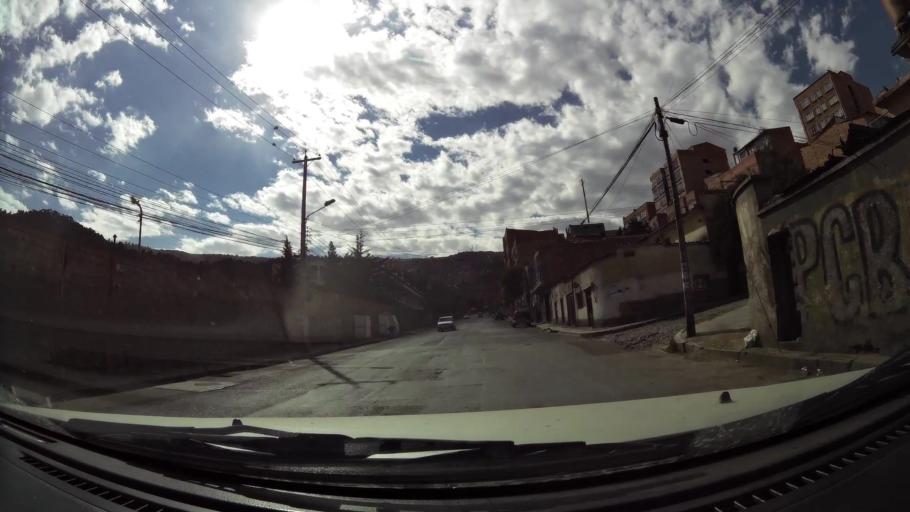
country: BO
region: La Paz
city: La Paz
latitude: -16.4764
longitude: -68.1507
